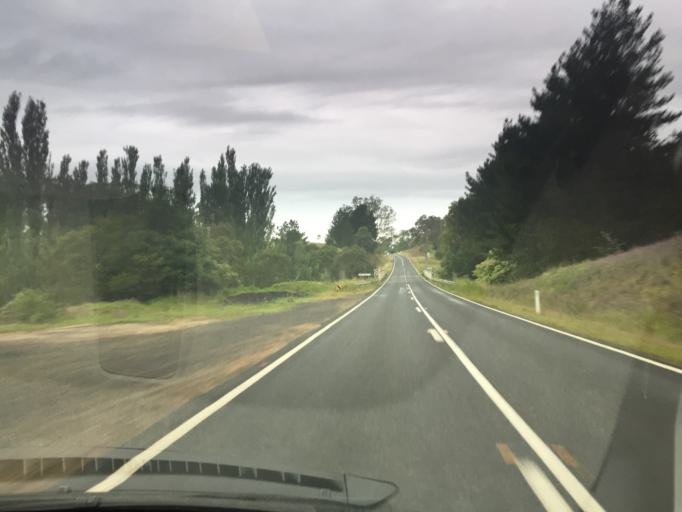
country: AU
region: New South Wales
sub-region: Bega Valley
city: Bega
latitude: -36.6406
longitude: 149.5827
